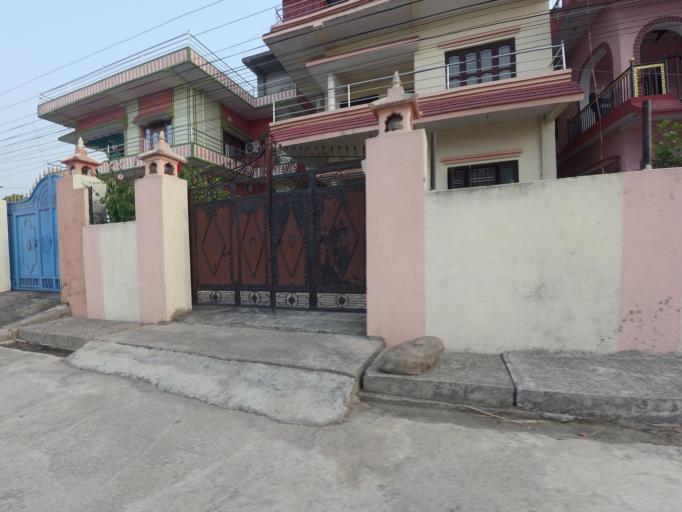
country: NP
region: Western Region
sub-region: Lumbini Zone
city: Bhairahawa
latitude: 27.5141
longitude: 83.4602
